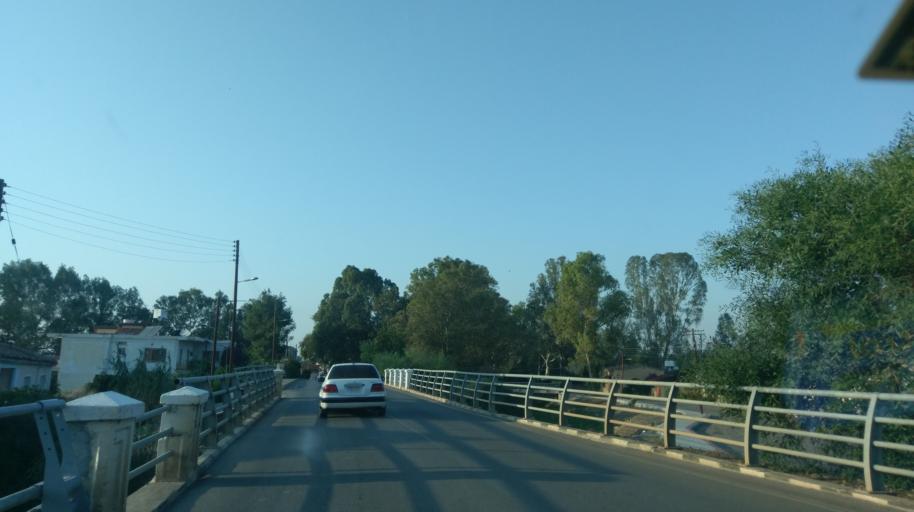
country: CY
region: Lefkosia
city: Astromeritis
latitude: 35.1642
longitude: 33.0135
